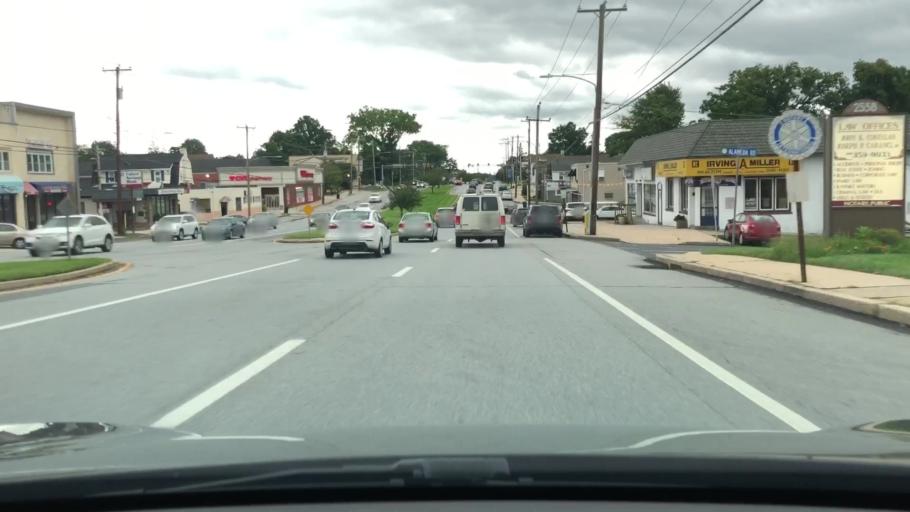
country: US
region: Pennsylvania
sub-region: Delaware County
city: Broomall
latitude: 39.9816
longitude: -75.3597
